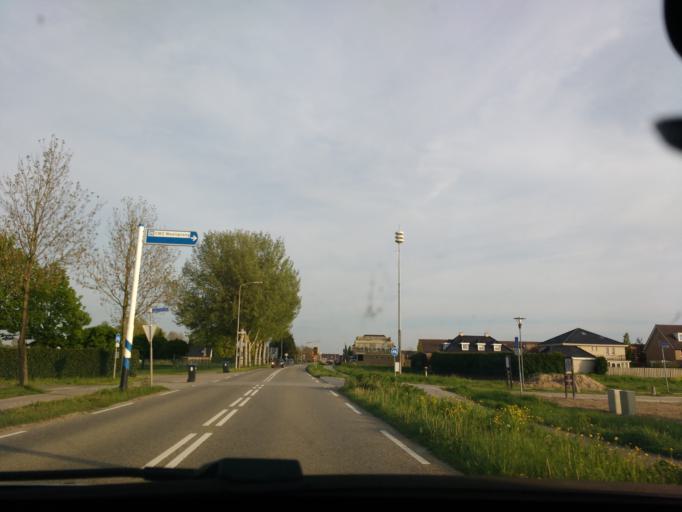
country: NL
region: Gelderland
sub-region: Gemeente Overbetuwe
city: Oosterhout
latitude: 51.8814
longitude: 5.8475
